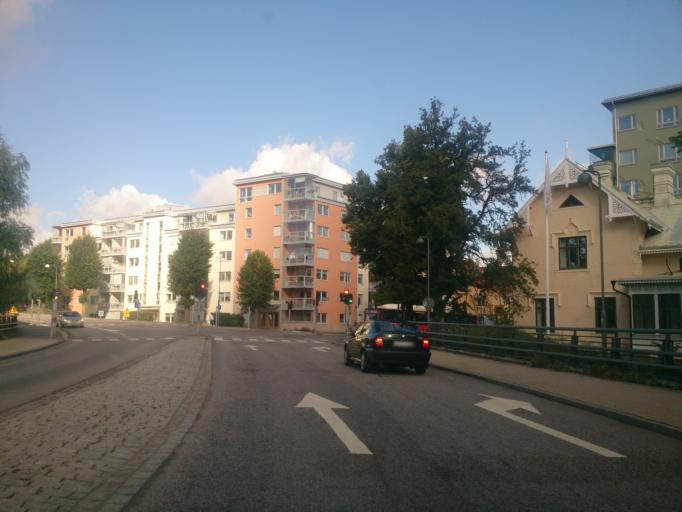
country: SE
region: OEstergoetland
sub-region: Linkopings Kommun
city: Linkoping
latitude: 58.4041
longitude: 15.6275
